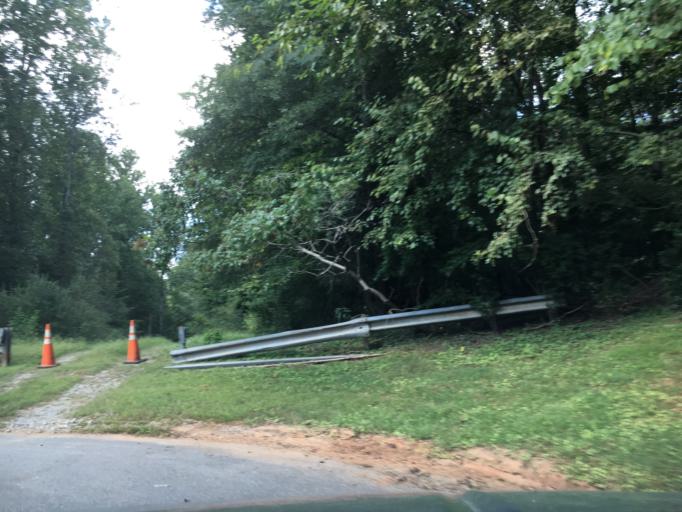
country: US
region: Virginia
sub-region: City of Lynchburg
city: West Lynchburg
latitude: 37.4229
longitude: -79.1739
